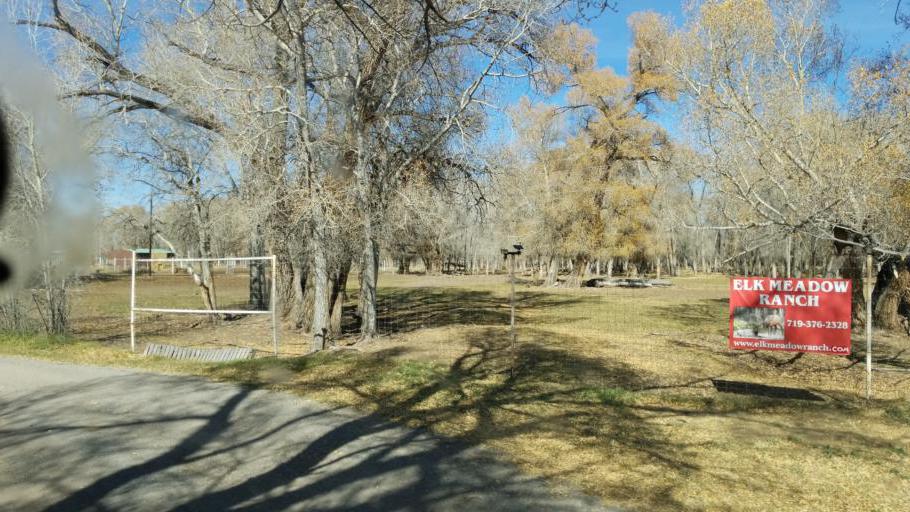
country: US
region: Colorado
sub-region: Conejos County
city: Conejos
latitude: 37.0603
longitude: -106.0945
